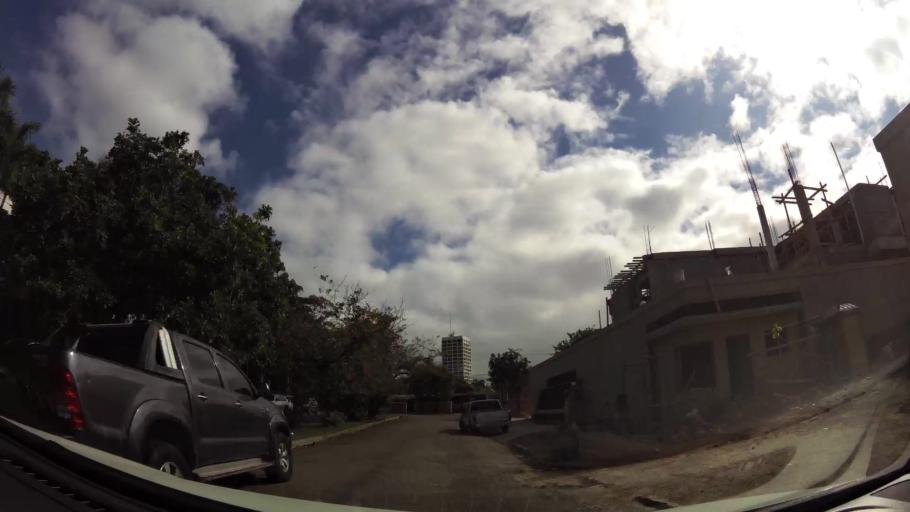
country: DO
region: Nacional
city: La Julia
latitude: 18.4622
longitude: -69.9261
